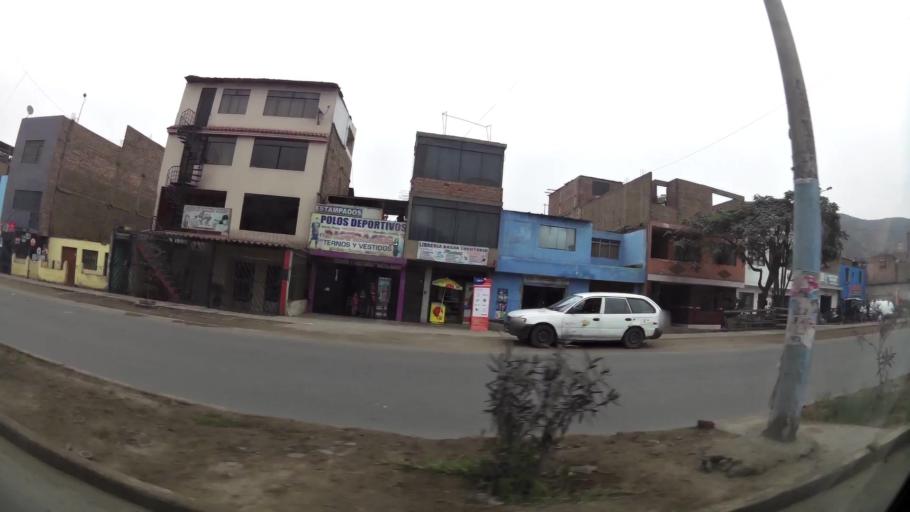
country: PE
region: Lima
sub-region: Lima
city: Urb. Santo Domingo
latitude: -11.9154
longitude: -77.0364
